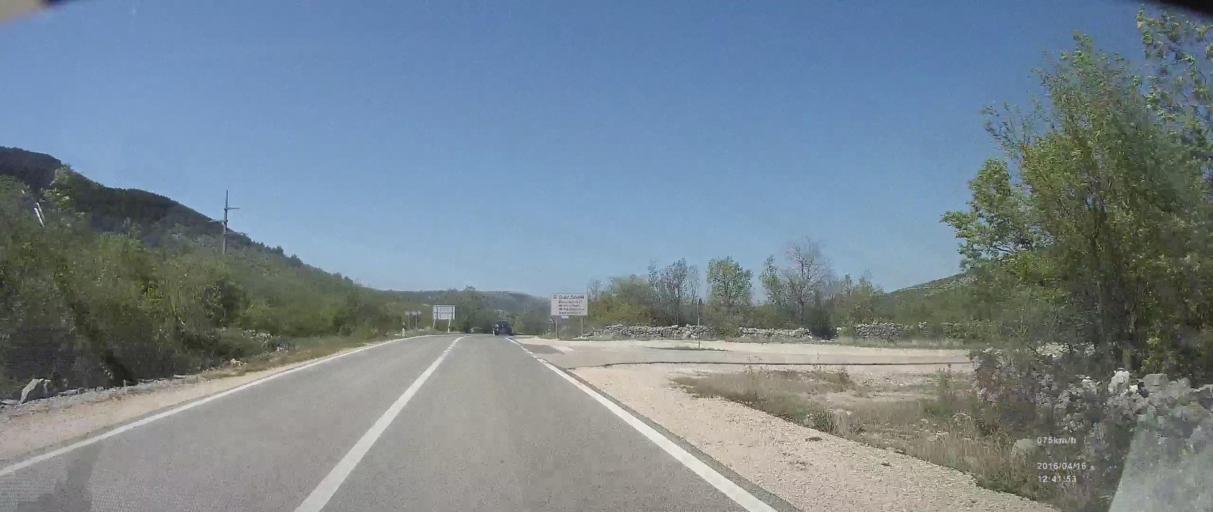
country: HR
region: Sibensko-Kniniska
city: Rogoznica
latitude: 43.6257
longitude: 16.0962
